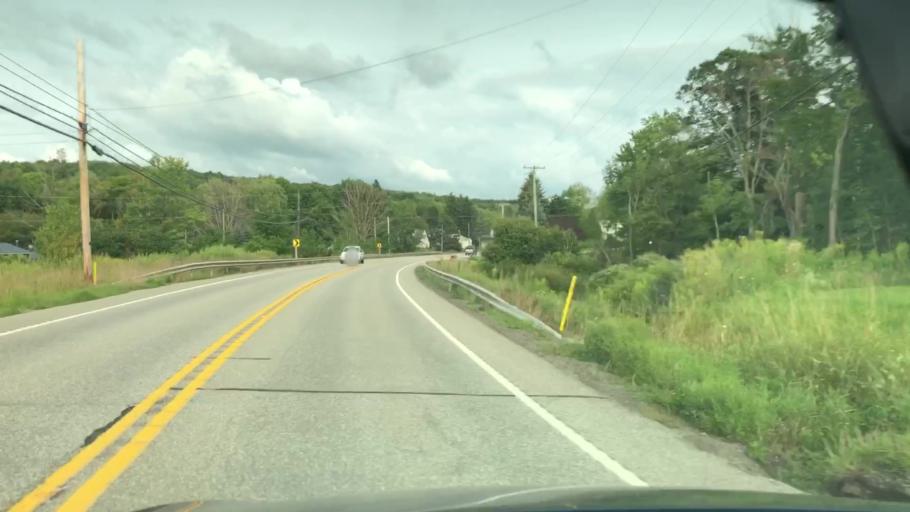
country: US
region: Pennsylvania
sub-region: Erie County
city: Northwest Harborcreek
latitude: 42.0683
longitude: -79.9540
